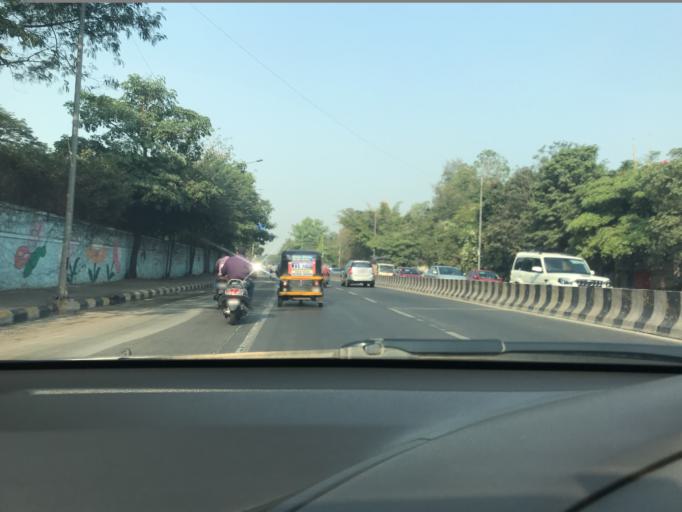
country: IN
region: Maharashtra
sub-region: Pune Division
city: Khadki
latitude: 18.5485
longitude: 73.8133
